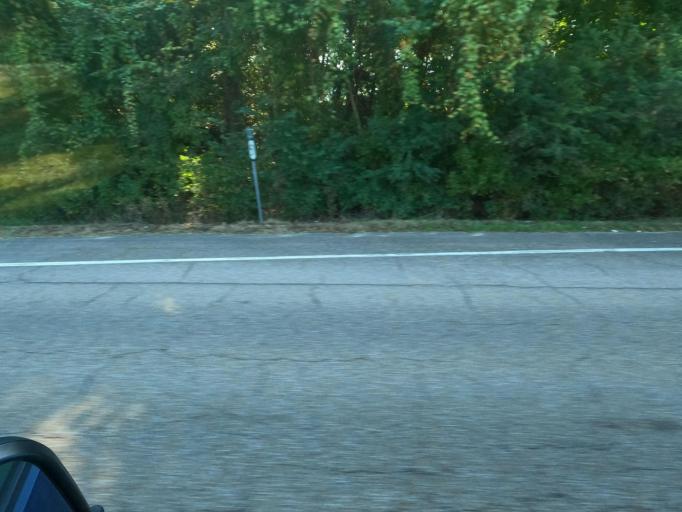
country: US
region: Tennessee
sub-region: Tipton County
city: Brighton
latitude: 35.4903
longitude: -89.7302
